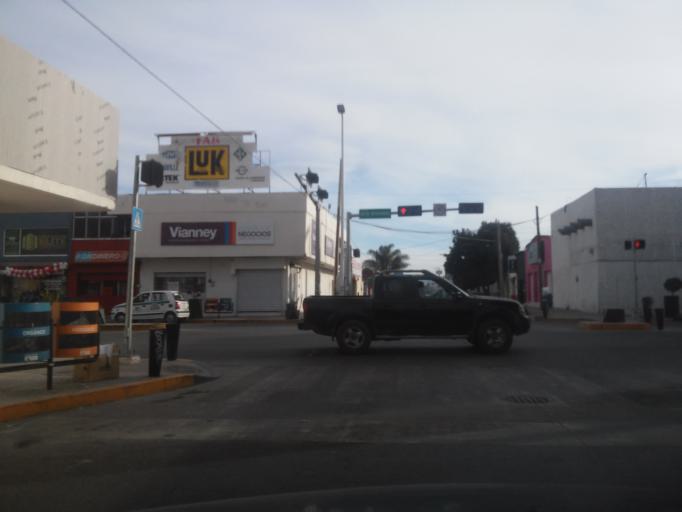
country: MX
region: Durango
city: Victoria de Durango
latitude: 24.0275
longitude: -104.6545
